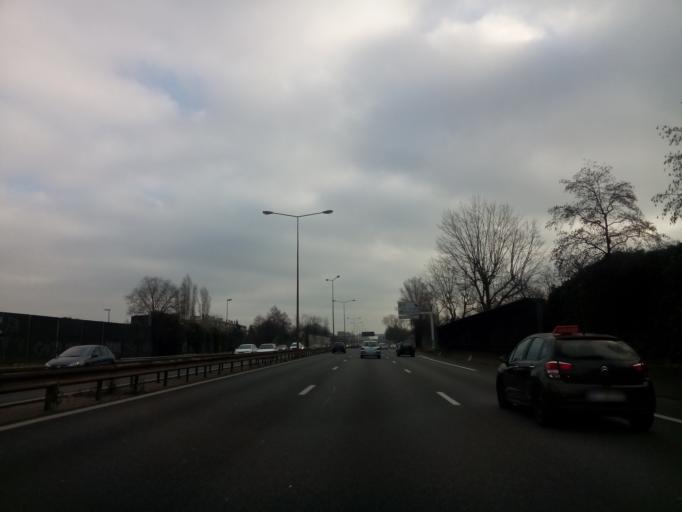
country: FR
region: Rhone-Alpes
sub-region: Departement du Rhone
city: Bron
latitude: 45.7269
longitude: 4.9125
